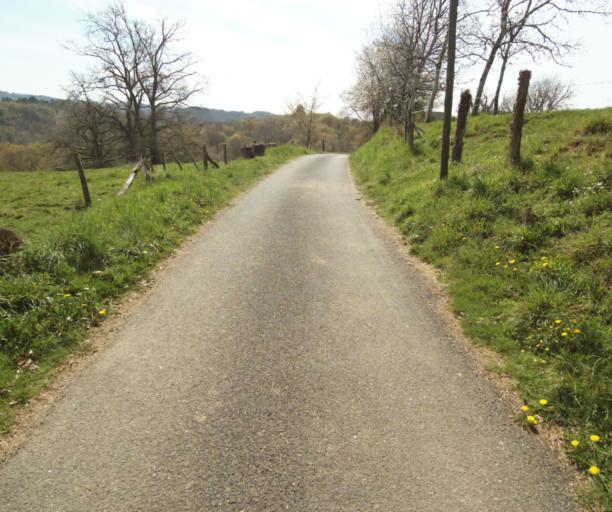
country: FR
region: Limousin
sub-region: Departement de la Correze
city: Naves
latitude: 45.3619
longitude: 1.8033
